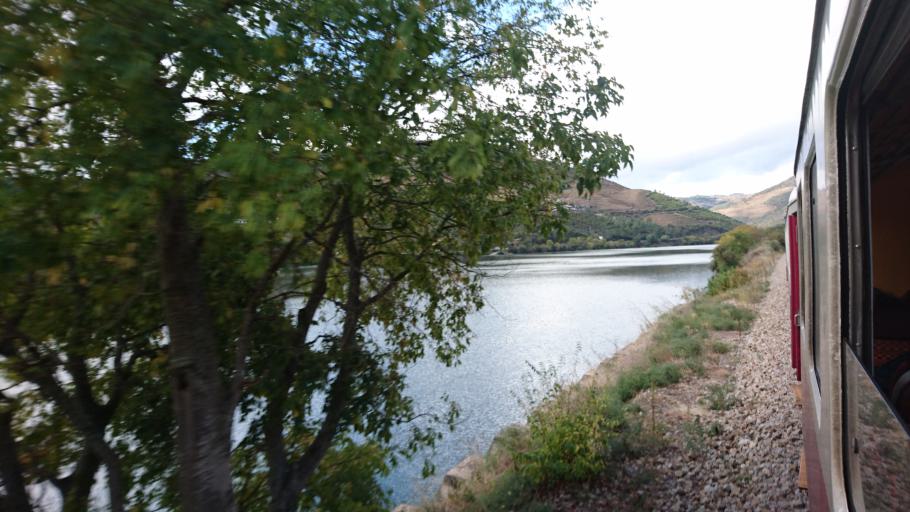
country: PT
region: Vila Real
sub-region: Sabrosa
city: Vilela
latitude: 41.1599
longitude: -7.6361
